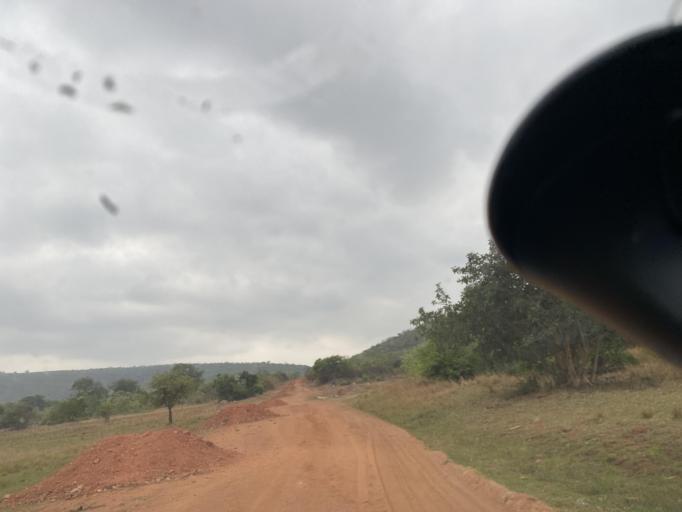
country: ZM
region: Lusaka
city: Chongwe
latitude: -15.1861
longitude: 28.7634
